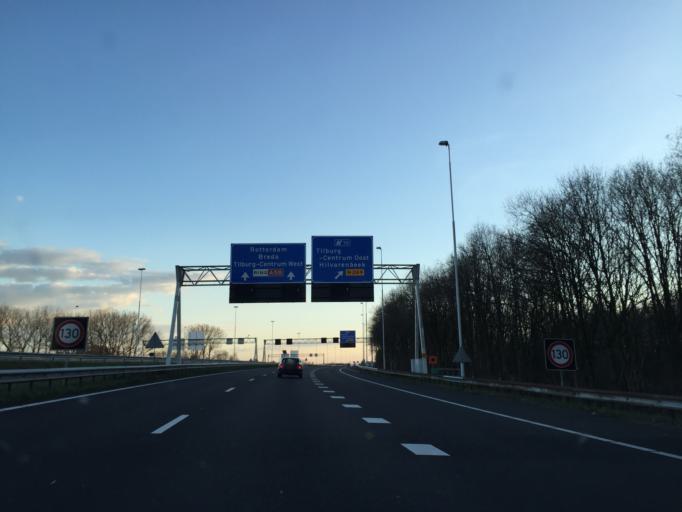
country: NL
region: North Brabant
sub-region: Gemeente Tilburg
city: Tilburg
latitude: 51.5491
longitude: 5.1204
